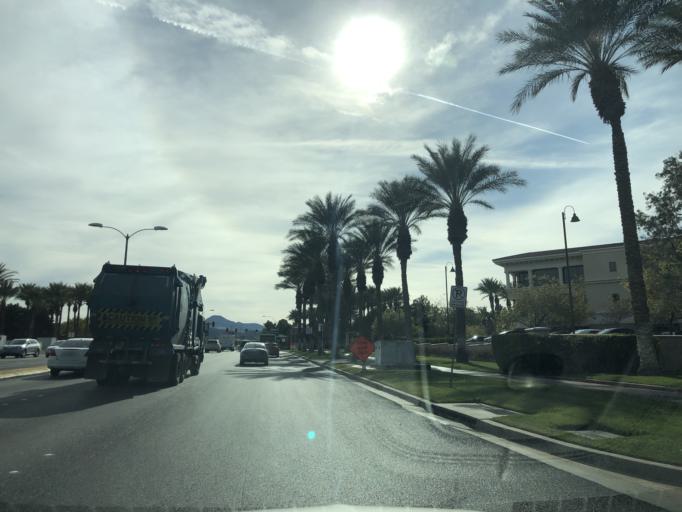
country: US
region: Nevada
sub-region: Clark County
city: Whitney
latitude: 36.0223
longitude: -115.0842
